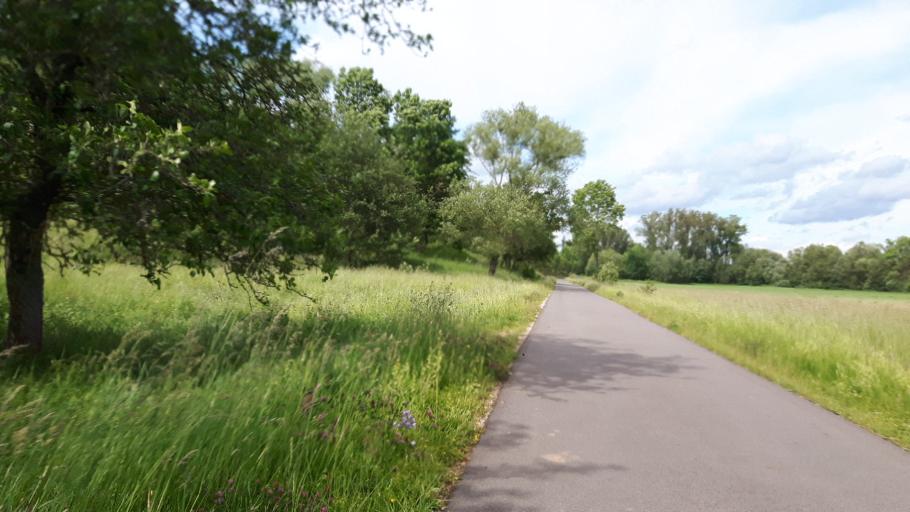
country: DE
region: Thuringia
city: Behringen
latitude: 50.7465
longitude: 11.0347
